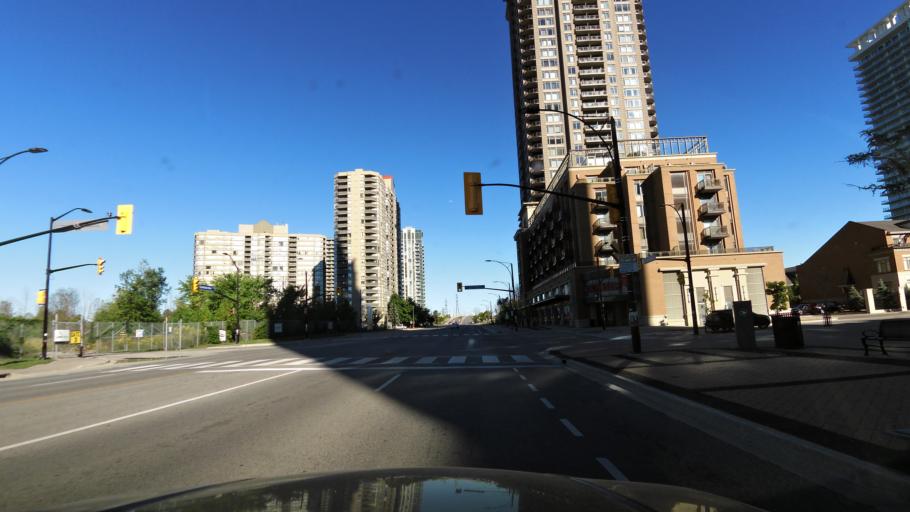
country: CA
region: Ontario
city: Mississauga
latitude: 43.5880
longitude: -79.6488
